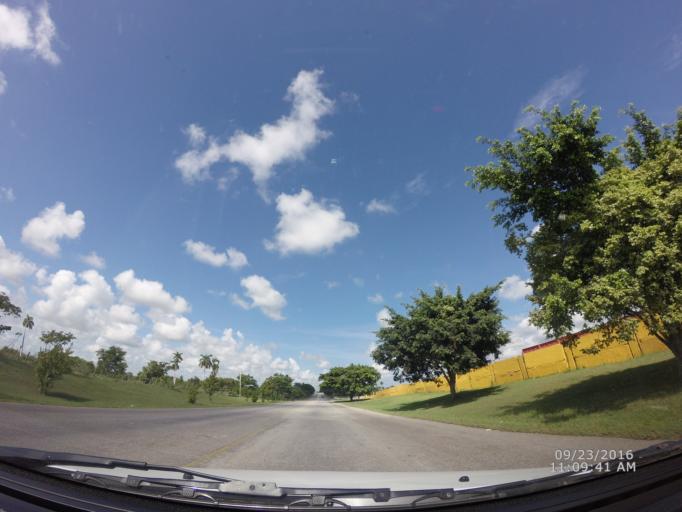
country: CU
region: La Habana
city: Arroyo Naranjo
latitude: 23.0187
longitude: -82.2482
